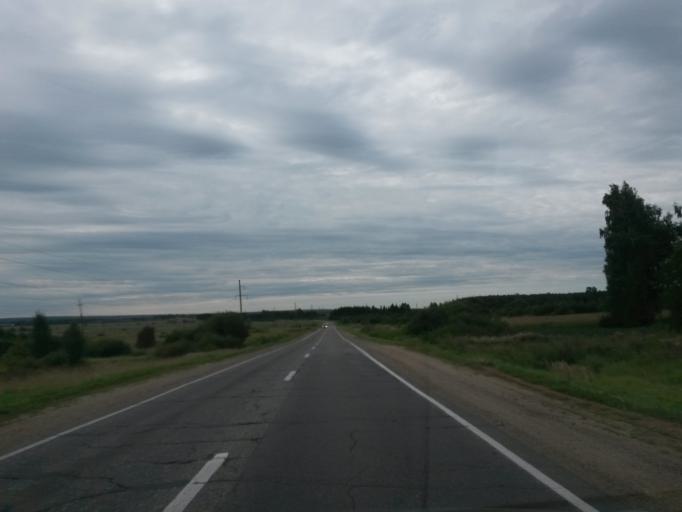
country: RU
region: Jaroslavl
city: Gavrilov-Yam
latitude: 57.3528
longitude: 39.7870
